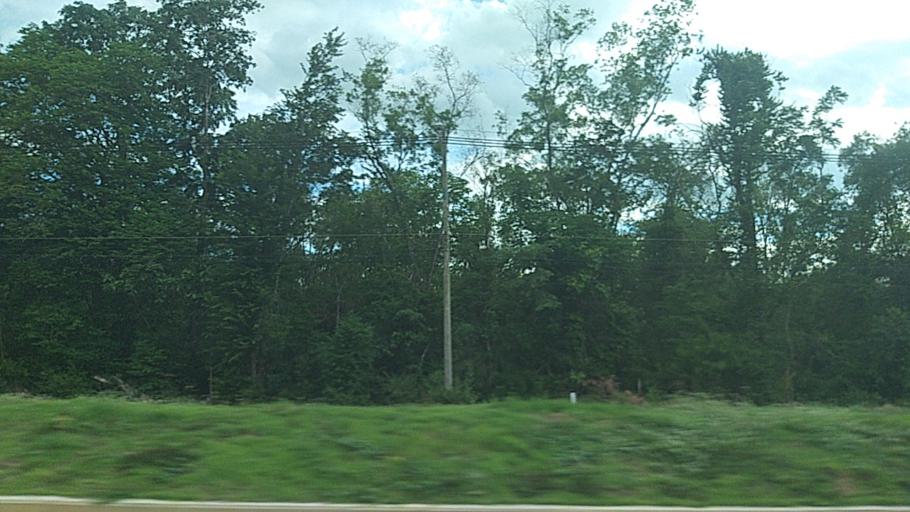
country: TH
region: Surin
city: Kap Choeng
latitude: 14.5512
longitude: 103.5090
